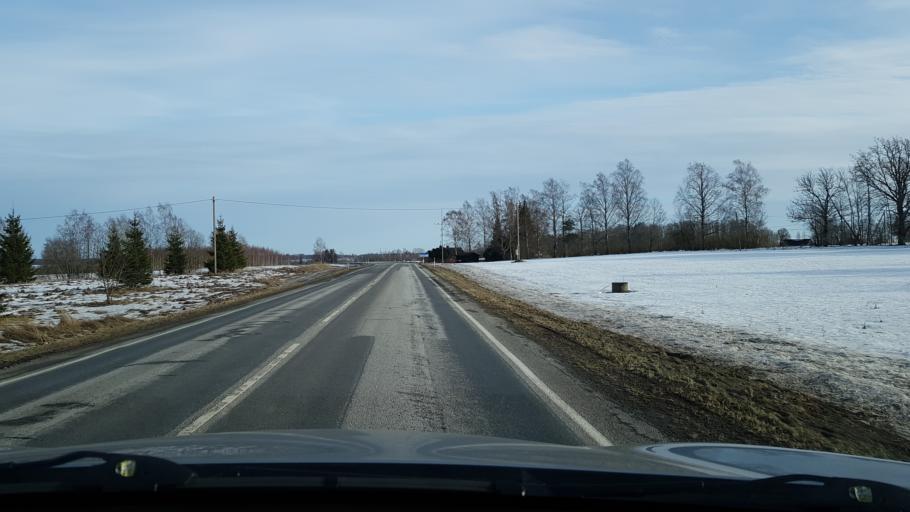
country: EE
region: Viljandimaa
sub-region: Viljandi linn
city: Viljandi
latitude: 58.3550
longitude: 25.4378
